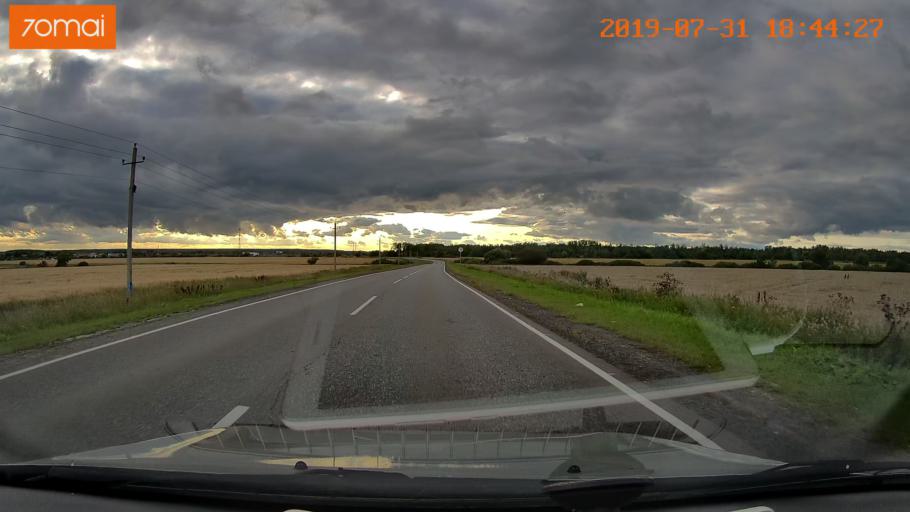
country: RU
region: Moskovskaya
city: Troitskoye
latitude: 55.2500
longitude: 38.5510
